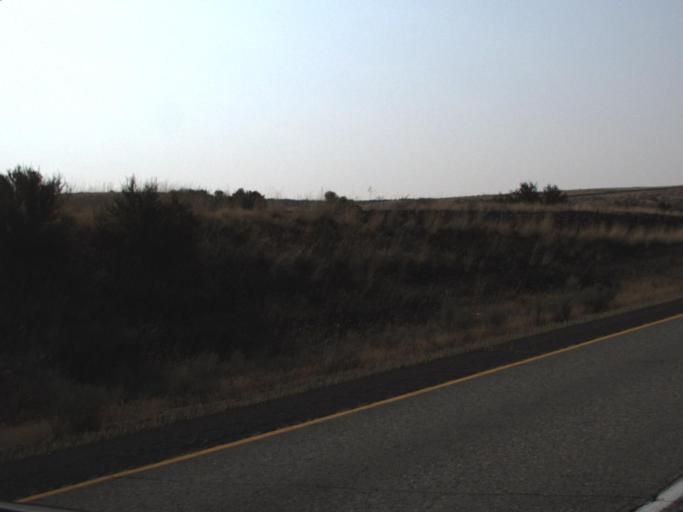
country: US
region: Washington
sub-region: Yakima County
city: Terrace Heights
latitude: 46.7734
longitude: -120.3763
